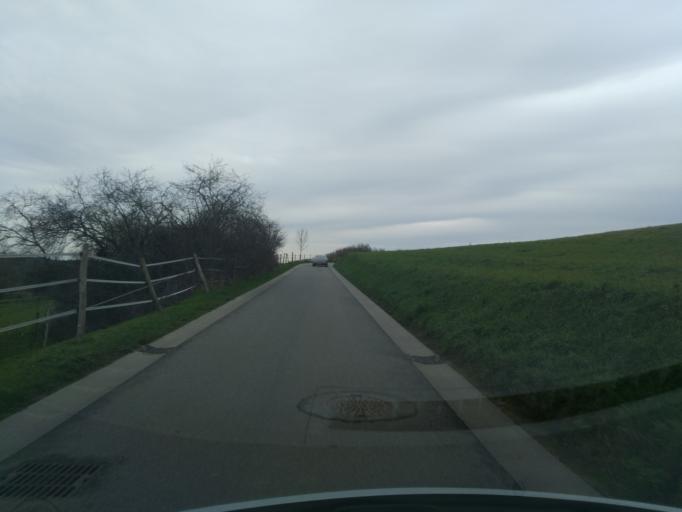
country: FR
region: Ile-de-France
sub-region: Departement des Yvelines
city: Chavenay
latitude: 48.8483
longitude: 1.9875
